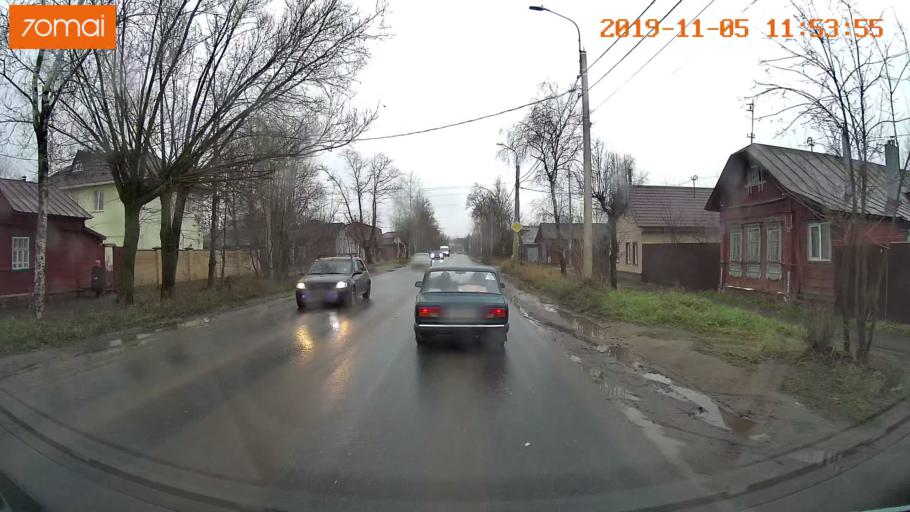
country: RU
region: Ivanovo
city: Bogorodskoye
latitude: 56.9940
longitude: 41.0307
